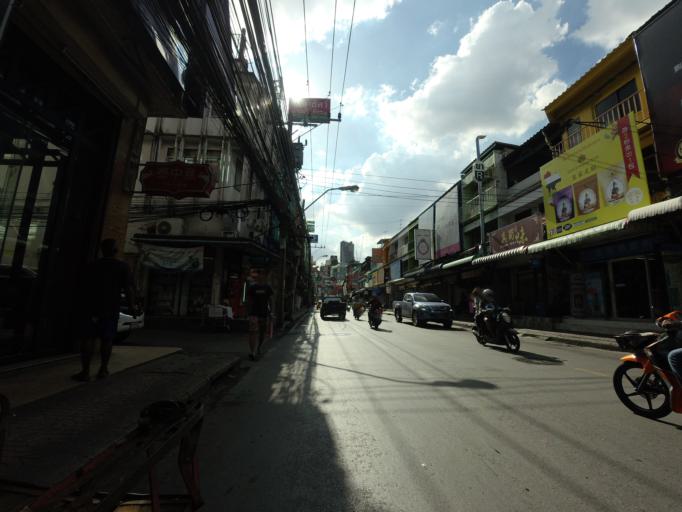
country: TH
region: Bangkok
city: Huai Khwang
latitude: 13.7781
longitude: 100.5780
